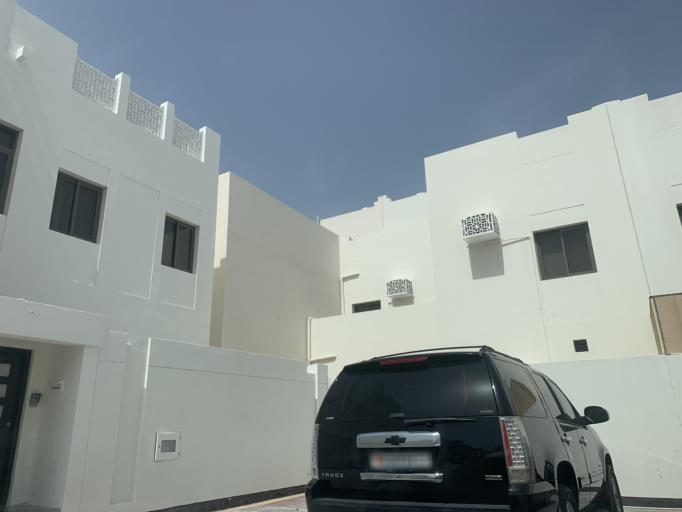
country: BH
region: Northern
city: Ar Rifa'
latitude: 26.1521
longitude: 50.5622
